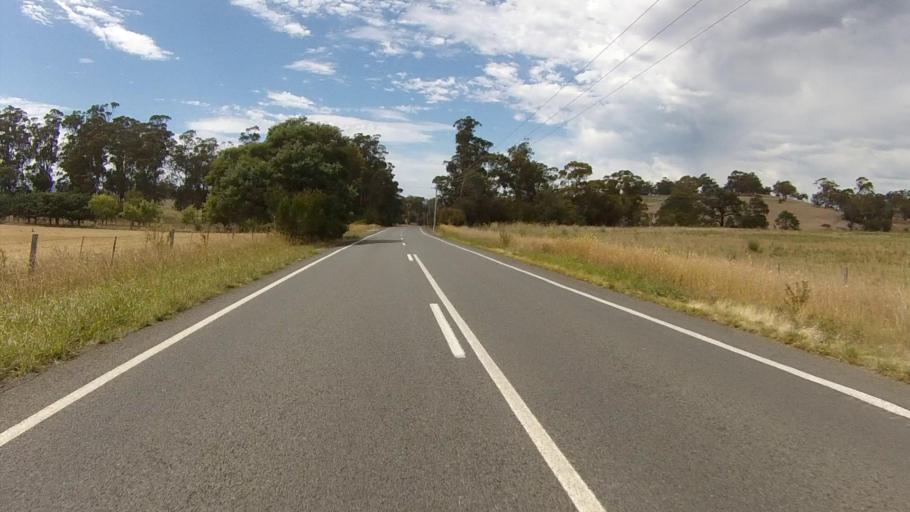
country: AU
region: Tasmania
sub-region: Clarence
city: Cambridge
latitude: -42.6755
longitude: 147.4013
